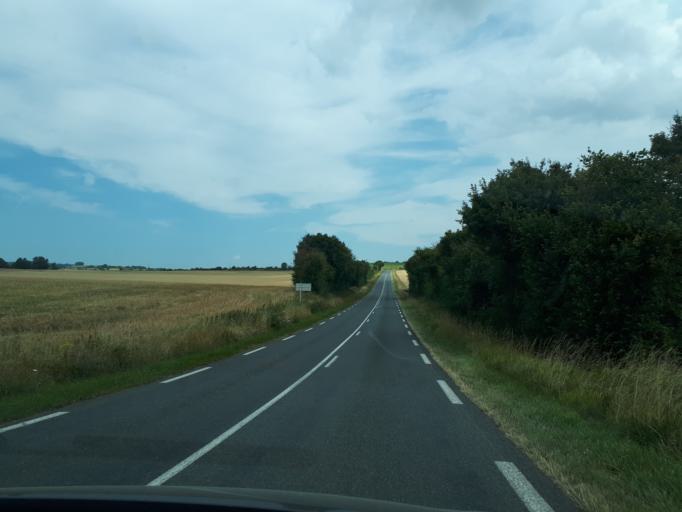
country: FR
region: Centre
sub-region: Departement du Cher
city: Rians
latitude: 47.2290
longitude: 2.6389
